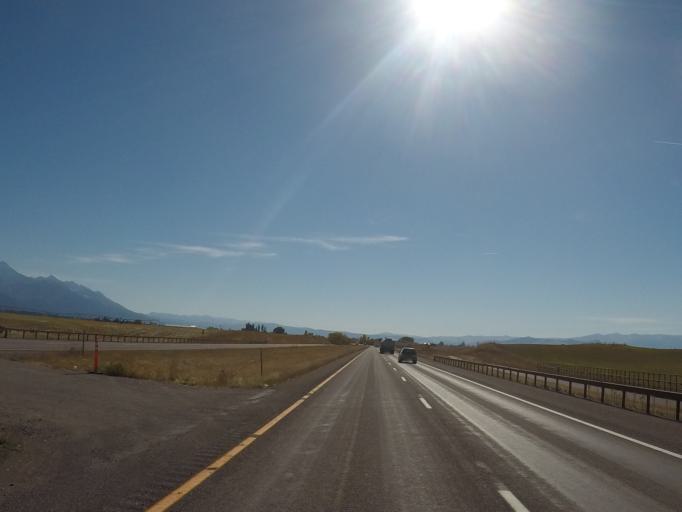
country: US
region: Montana
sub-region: Lake County
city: Ronan
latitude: 47.5550
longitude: -114.1132
